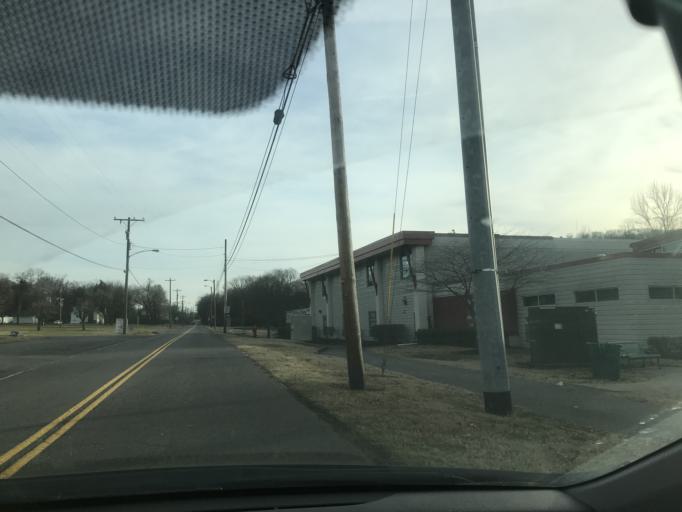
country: US
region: Tennessee
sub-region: Davidson County
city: Nashville
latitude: 36.2100
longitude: -86.8237
